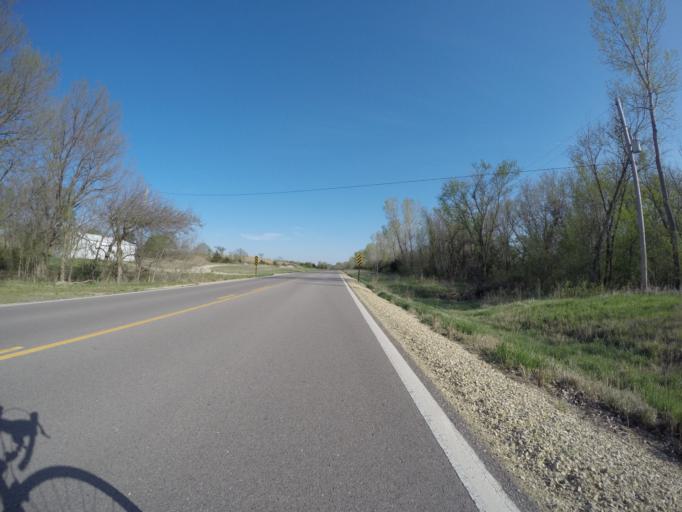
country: US
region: Kansas
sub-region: Riley County
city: Fort Riley North
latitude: 39.2399
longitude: -96.7625
